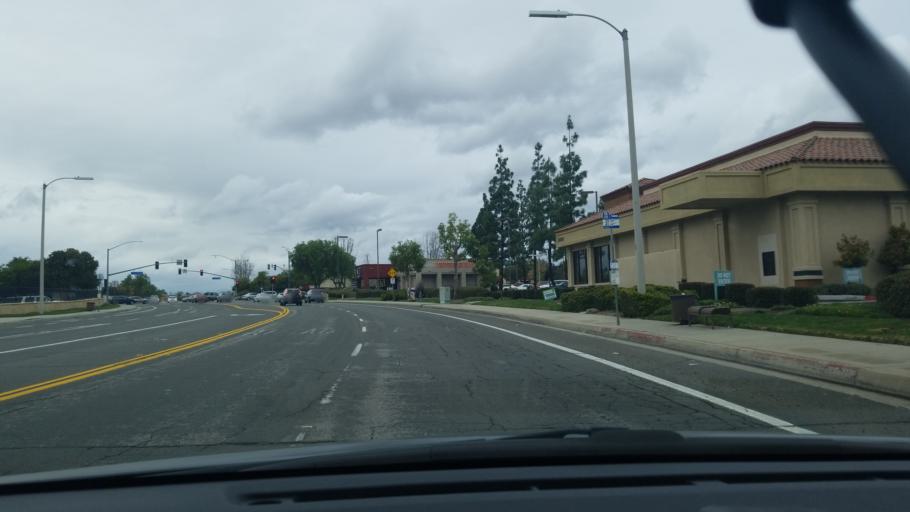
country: US
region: California
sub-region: Riverside County
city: Murrieta Hot Springs
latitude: 33.5698
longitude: -117.1829
